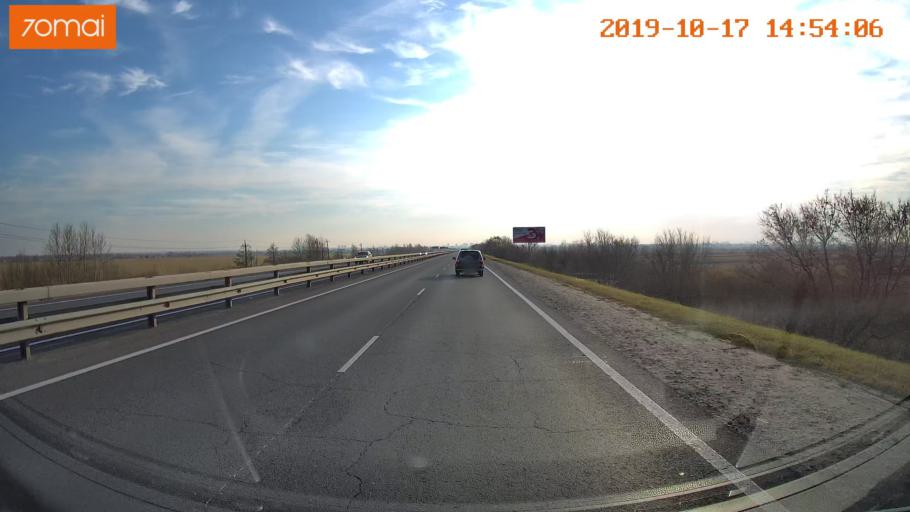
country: RU
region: Rjazan
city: Polyany
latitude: 54.6859
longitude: 39.8344
